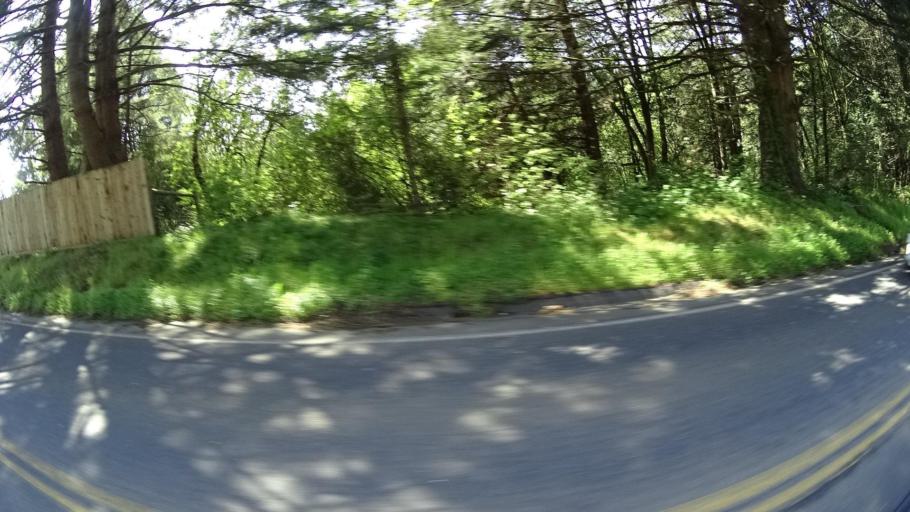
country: US
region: California
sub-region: Humboldt County
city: Hydesville
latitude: 40.5538
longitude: -124.1046
